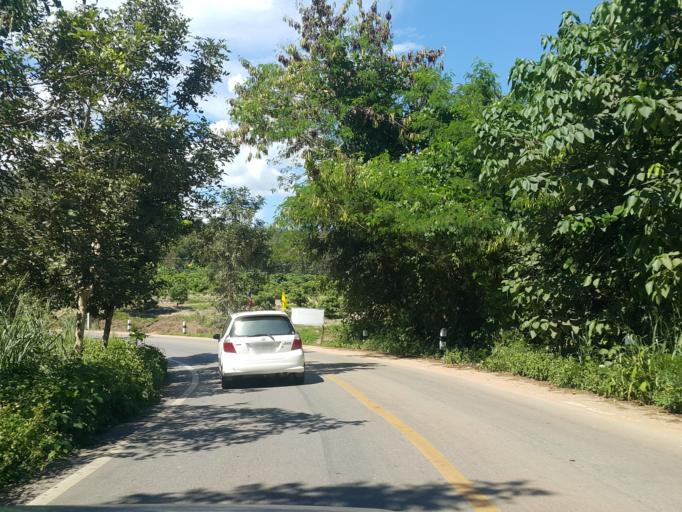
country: TH
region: Chiang Mai
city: Mae Taeng
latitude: 19.1784
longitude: 98.9161
